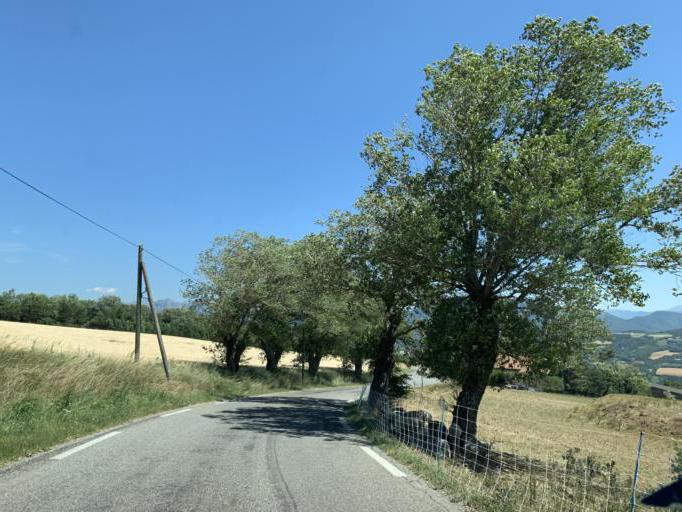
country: FR
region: Provence-Alpes-Cote d'Azur
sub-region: Departement des Hautes-Alpes
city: La Batie-Neuve
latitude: 44.5916
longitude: 6.1536
